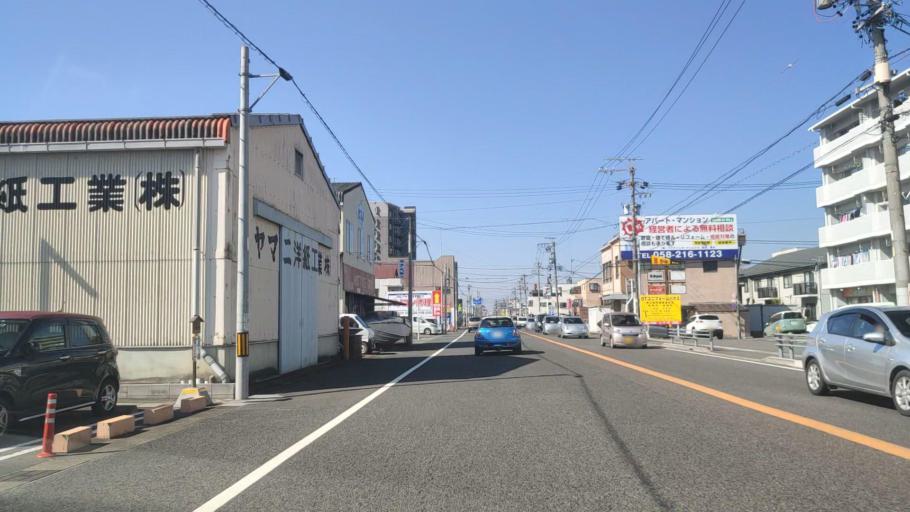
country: JP
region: Gifu
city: Gifu-shi
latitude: 35.3972
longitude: 136.7676
